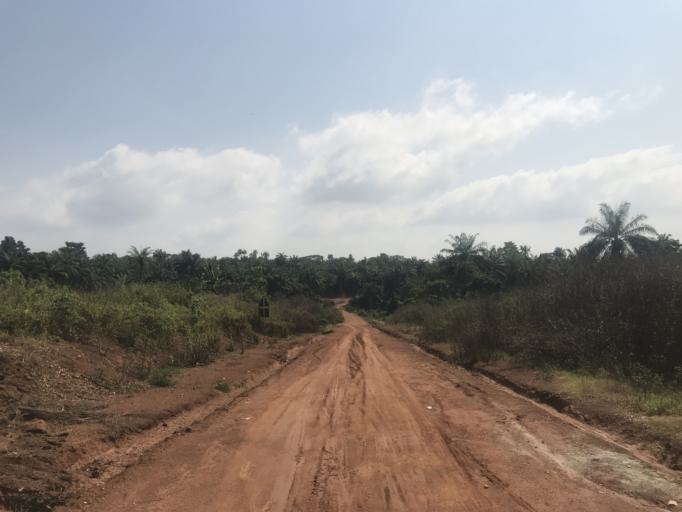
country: NG
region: Osun
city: Ikirun
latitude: 7.8364
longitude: 4.6287
